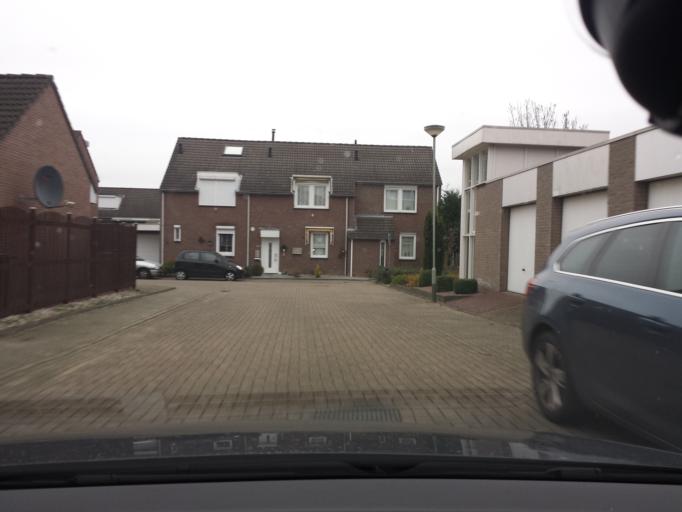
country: NL
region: Limburg
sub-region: Gemeente Kerkrade
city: Kerkrade
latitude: 50.9101
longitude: 6.0315
